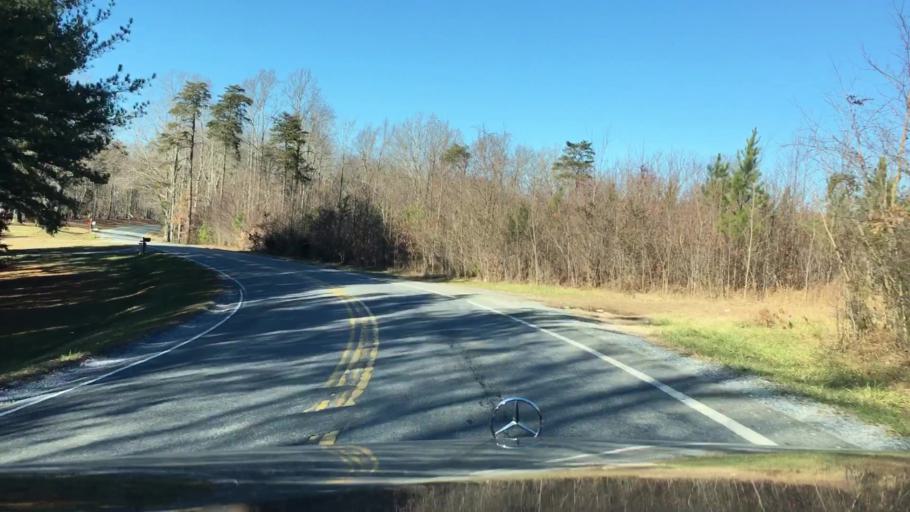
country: US
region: Virginia
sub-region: Pittsylvania County
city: Motley
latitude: 37.1687
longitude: -79.4053
